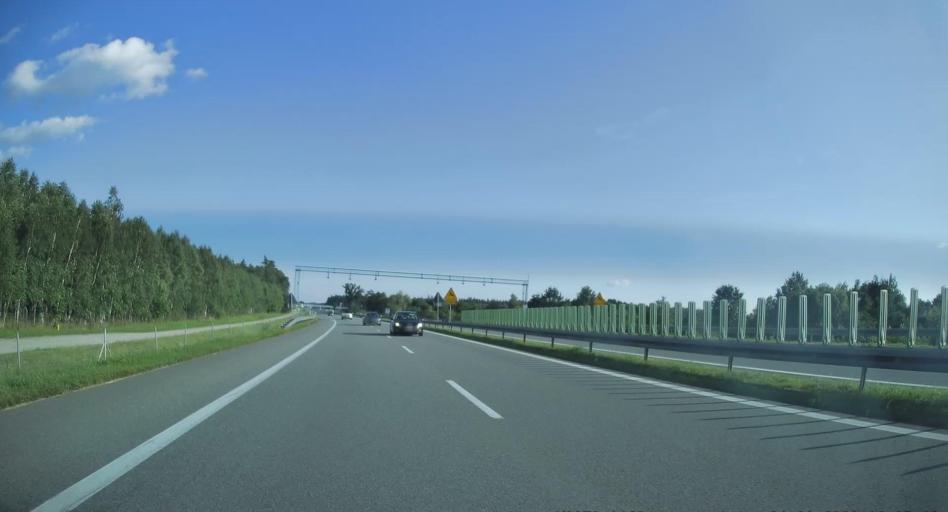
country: PL
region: Masovian Voivodeship
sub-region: Powiat bialobrzeski
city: Sucha
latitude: 51.6280
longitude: 20.9698
